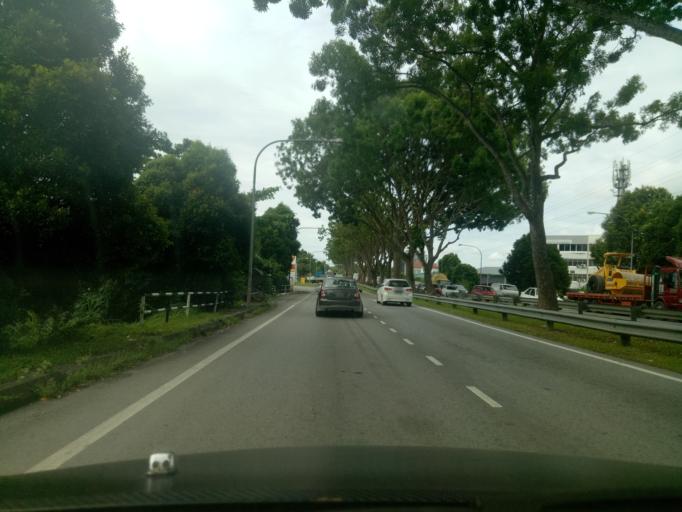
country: MY
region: Sarawak
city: Kuching
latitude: 1.5385
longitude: 110.3689
